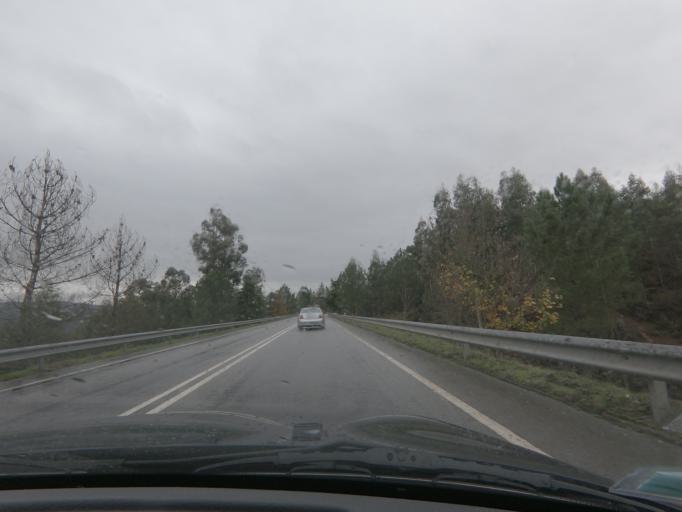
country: PT
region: Porto
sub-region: Amarante
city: Amarante
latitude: 41.3281
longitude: -8.0409
